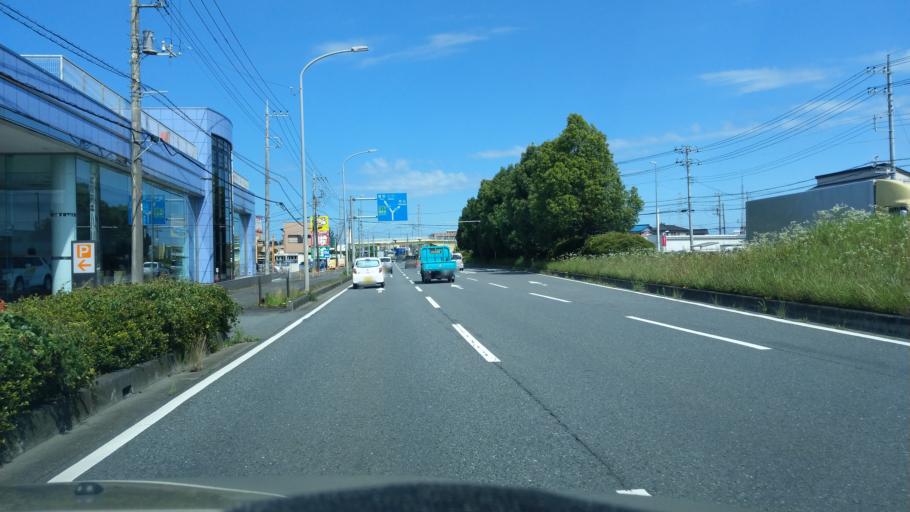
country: JP
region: Saitama
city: Sakado
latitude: 36.0172
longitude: 139.4298
